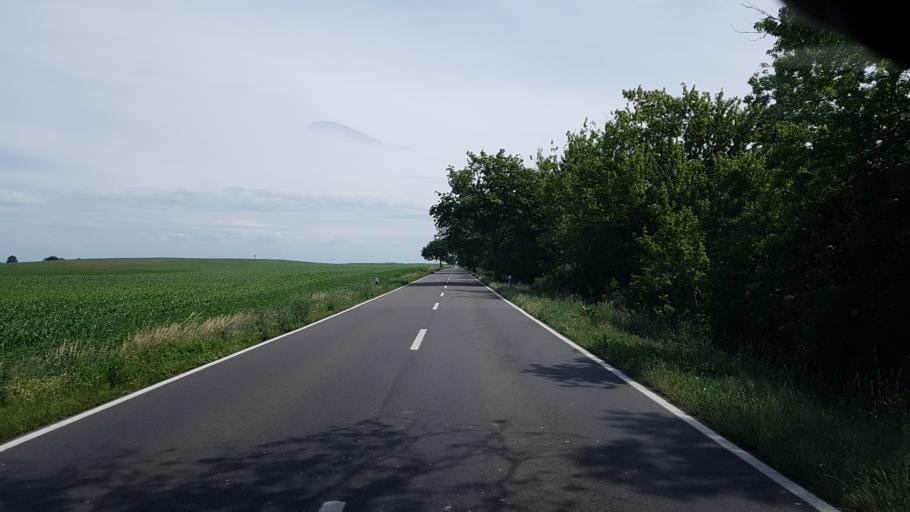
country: DE
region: Brandenburg
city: Prenzlau
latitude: 53.3770
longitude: 13.7834
